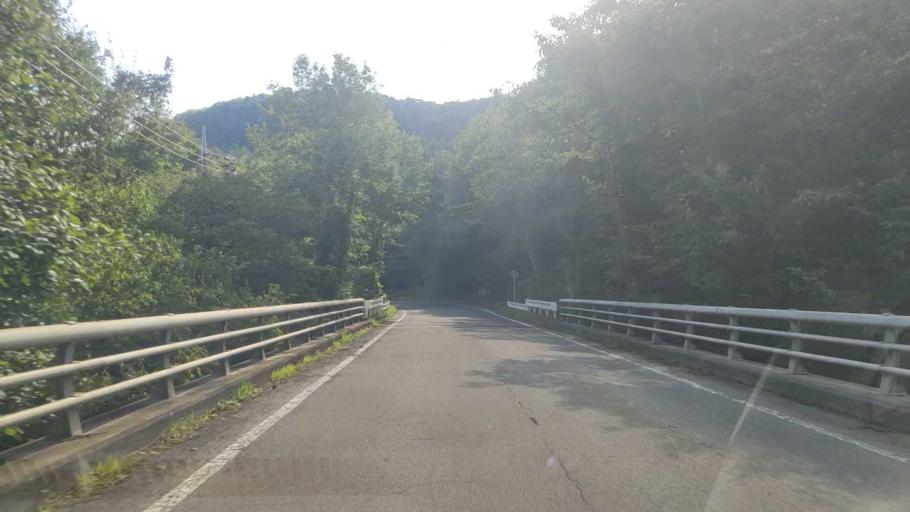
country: JP
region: Nagano
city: Suzaka
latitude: 36.5704
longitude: 138.5566
